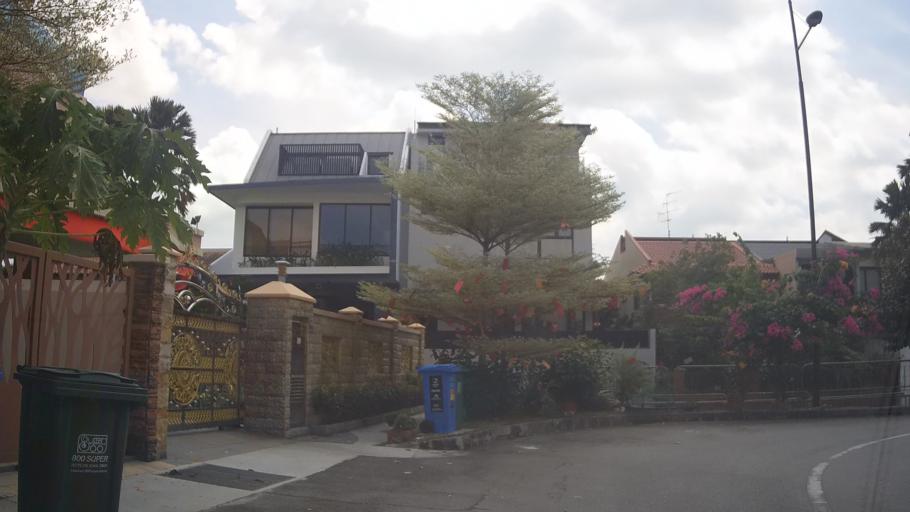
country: SG
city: Singapore
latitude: 1.3250
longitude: 103.9553
